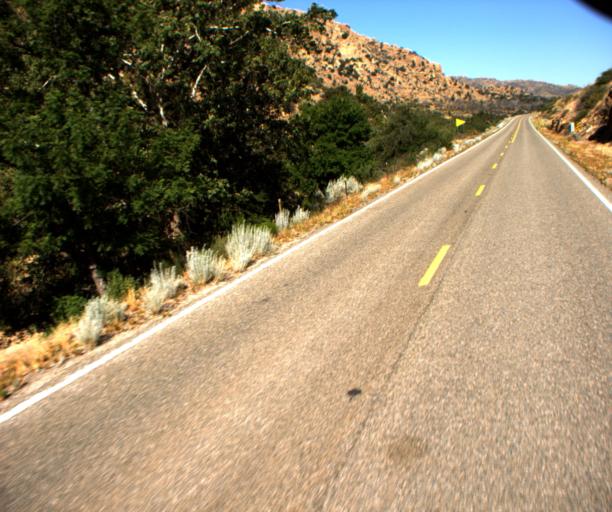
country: US
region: Arizona
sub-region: Graham County
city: Swift Trail Junction
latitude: 32.5628
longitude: -109.7960
